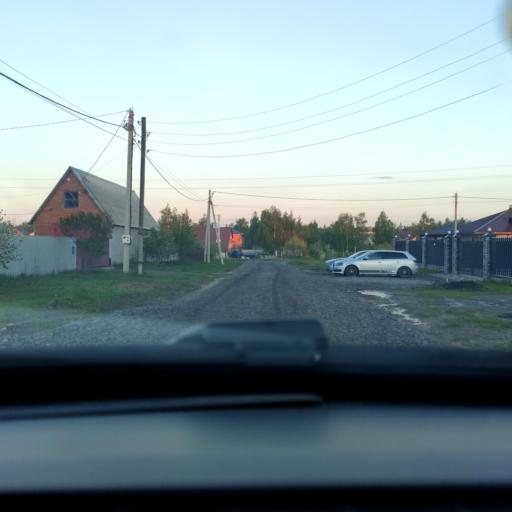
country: RU
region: Voronezj
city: Novaya Usman'
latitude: 51.6555
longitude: 39.4231
